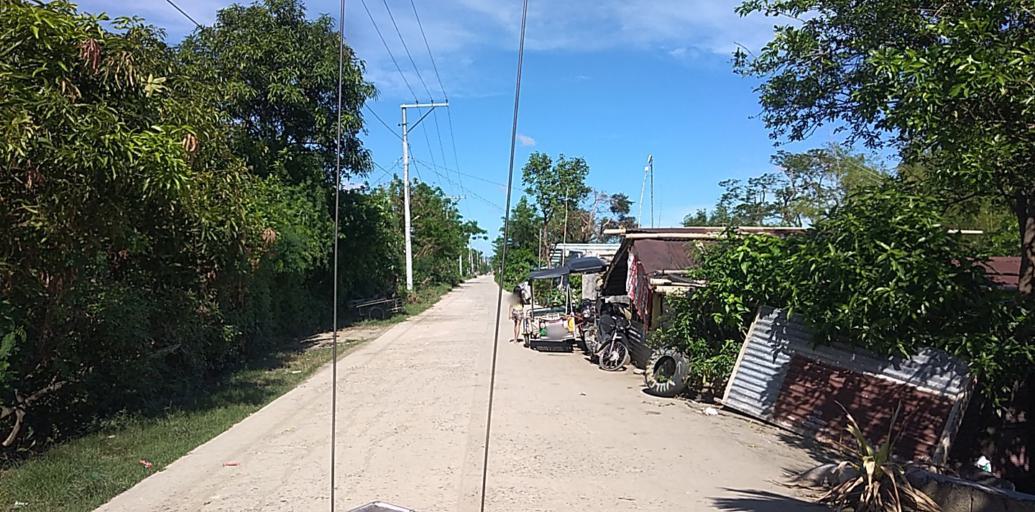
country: PH
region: Central Luzon
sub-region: Province of Pampanga
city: Candating
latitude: 15.1234
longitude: 120.8122
